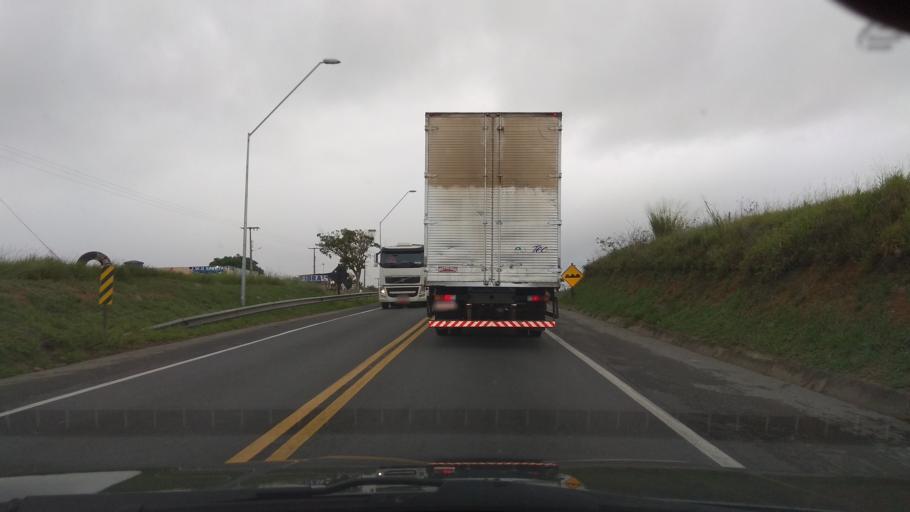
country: BR
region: Bahia
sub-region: Jaguaquara
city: Jaguaquara
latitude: -13.4789
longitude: -40.0414
